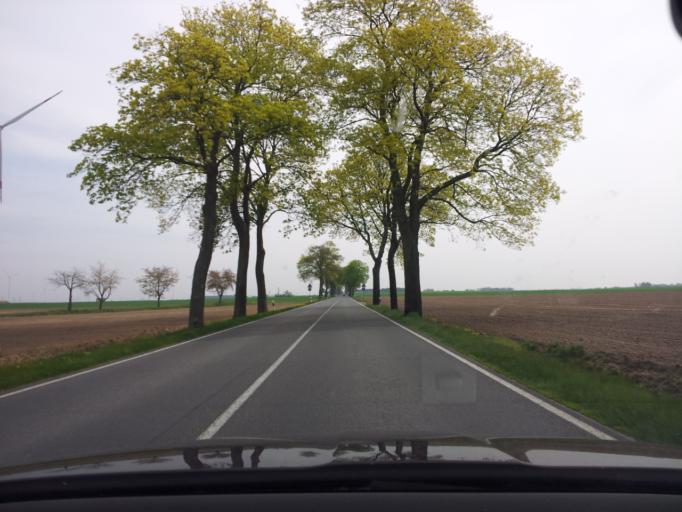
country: DE
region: Brandenburg
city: Luckau
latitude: 51.8745
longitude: 13.7614
